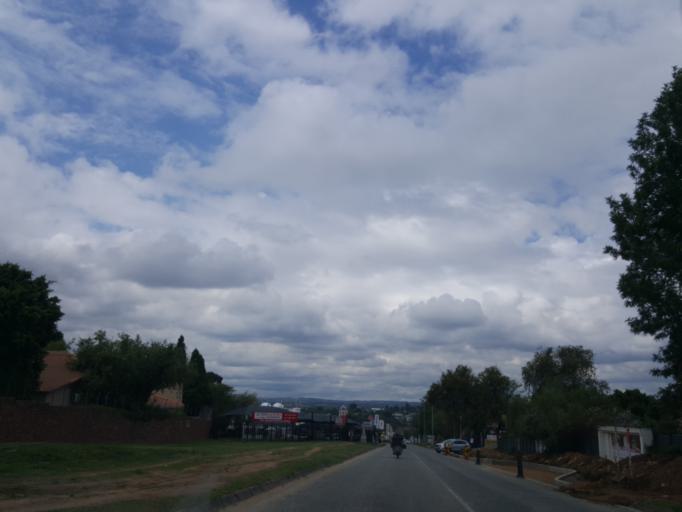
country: ZA
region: Gauteng
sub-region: City of Johannesburg Metropolitan Municipality
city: Diepsloot
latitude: -26.0103
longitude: 28.0007
